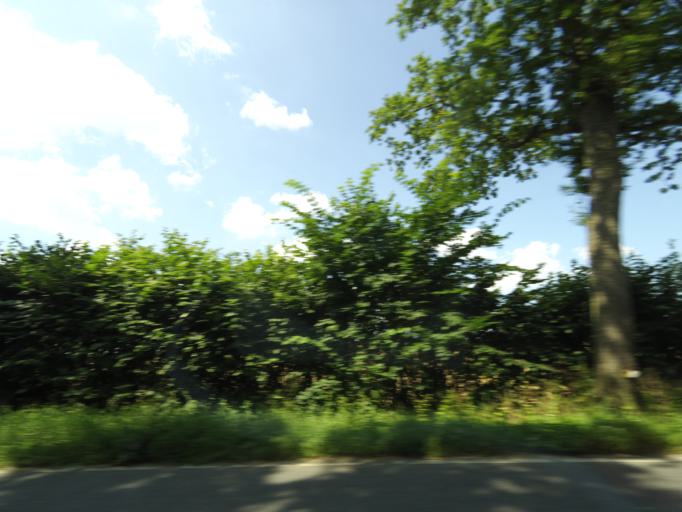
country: DK
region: South Denmark
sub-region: Assens Kommune
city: Arup
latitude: 55.3971
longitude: 10.0440
